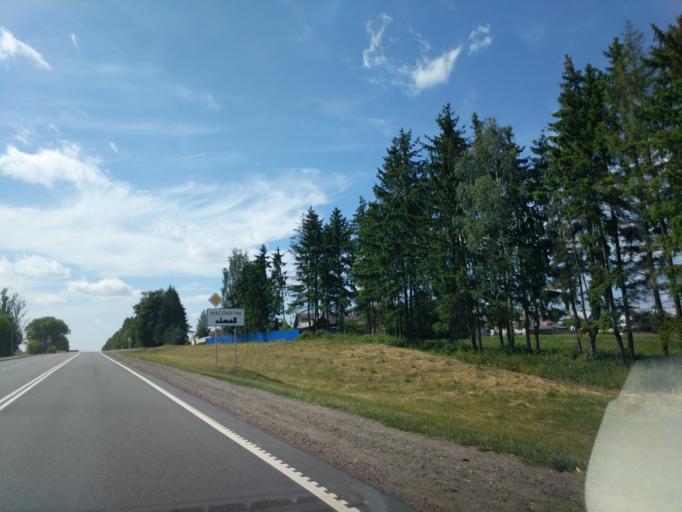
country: BY
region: Minsk
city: Syomkava
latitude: 54.0960
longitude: 27.5042
